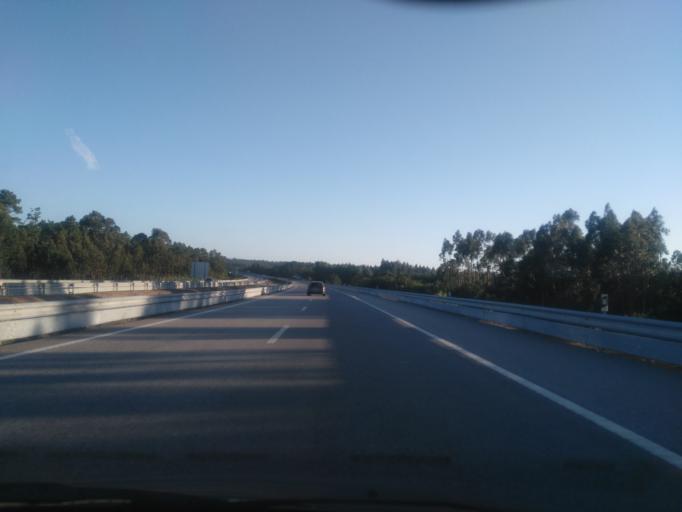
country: PT
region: Coimbra
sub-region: Figueira da Foz
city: Alhadas
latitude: 40.2085
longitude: -8.8134
